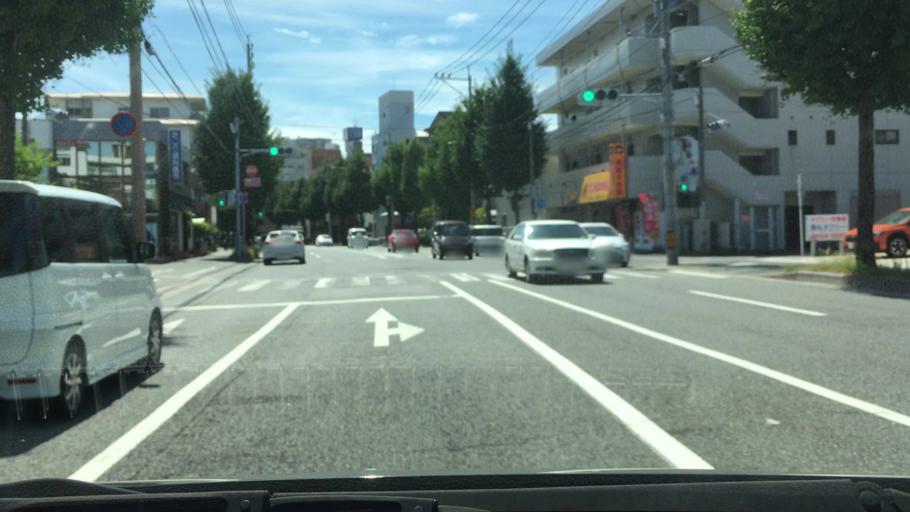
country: JP
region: Fukuoka
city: Fukuoka-shi
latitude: 33.5653
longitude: 130.4287
